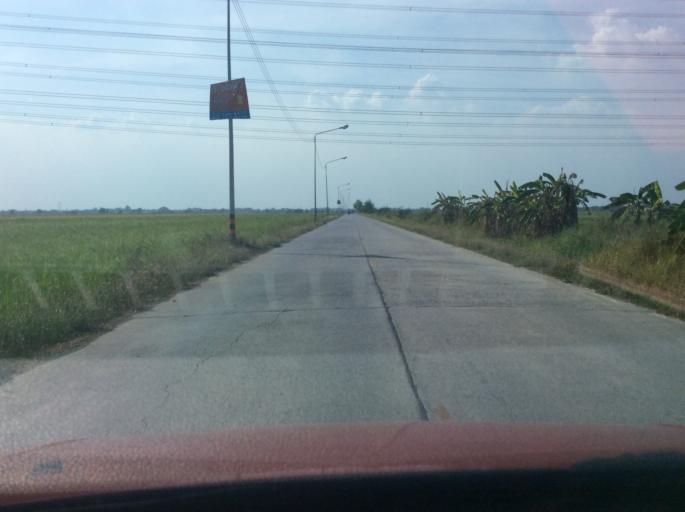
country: TH
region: Pathum Thani
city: Ban Lam Luk Ka
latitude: 13.9860
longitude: 100.7719
